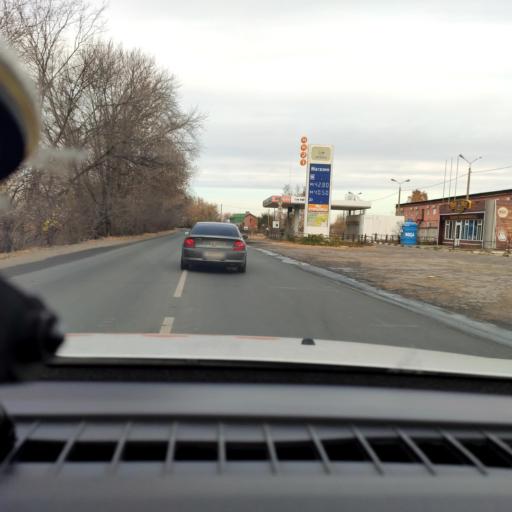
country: RU
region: Samara
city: Novokuybyshevsk
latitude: 53.1447
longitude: 50.0301
